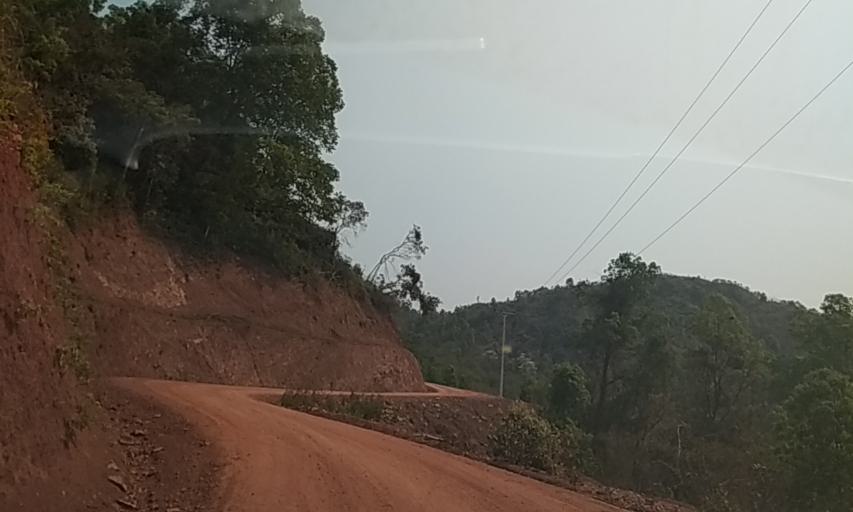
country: VN
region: Huyen Dien Bien
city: Dien Bien Phu
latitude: 21.4572
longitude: 102.7712
